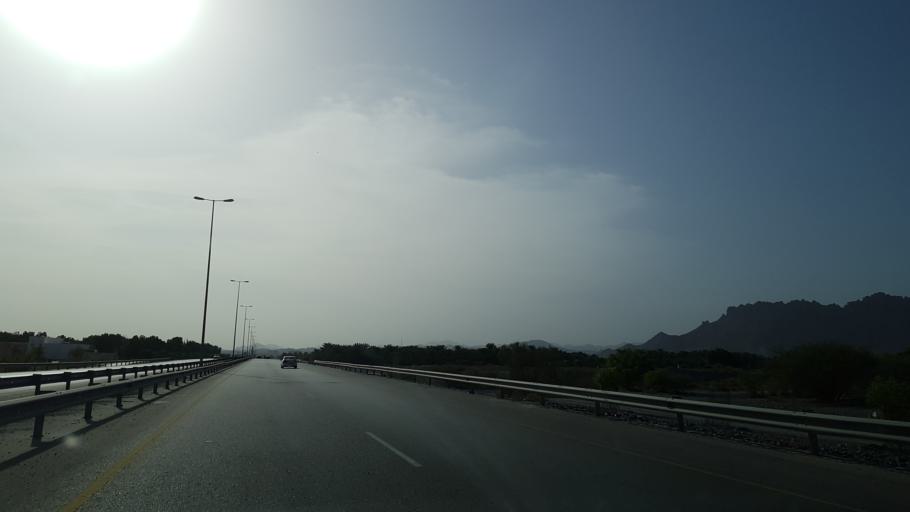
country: OM
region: Muhafazat ad Dakhiliyah
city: Nizwa
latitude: 22.8580
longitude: 57.5660
